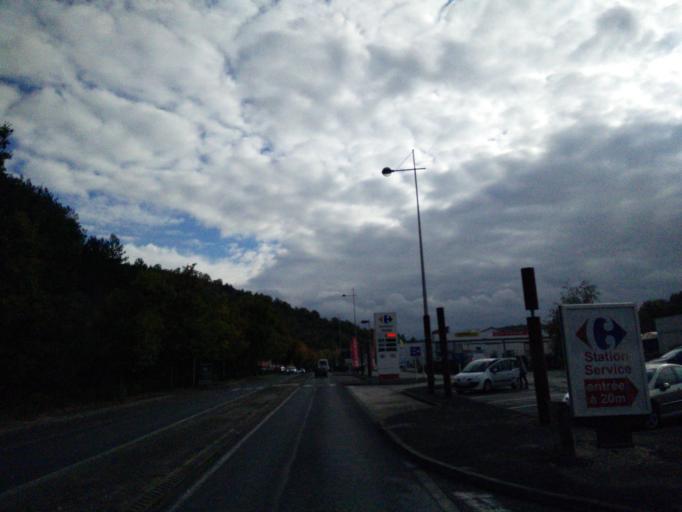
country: FR
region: Midi-Pyrenees
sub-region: Departement du Lot
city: Cahors
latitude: 44.4207
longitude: 1.4392
